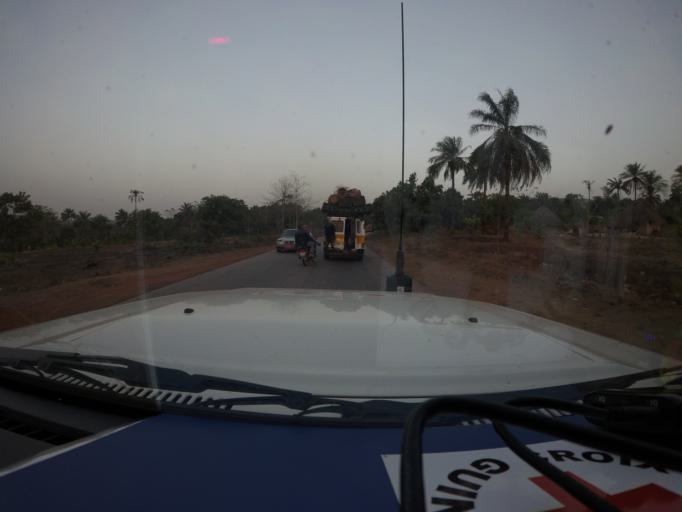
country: GN
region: Kindia
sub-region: Kindia
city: Kindia
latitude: 9.9012
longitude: -13.0268
